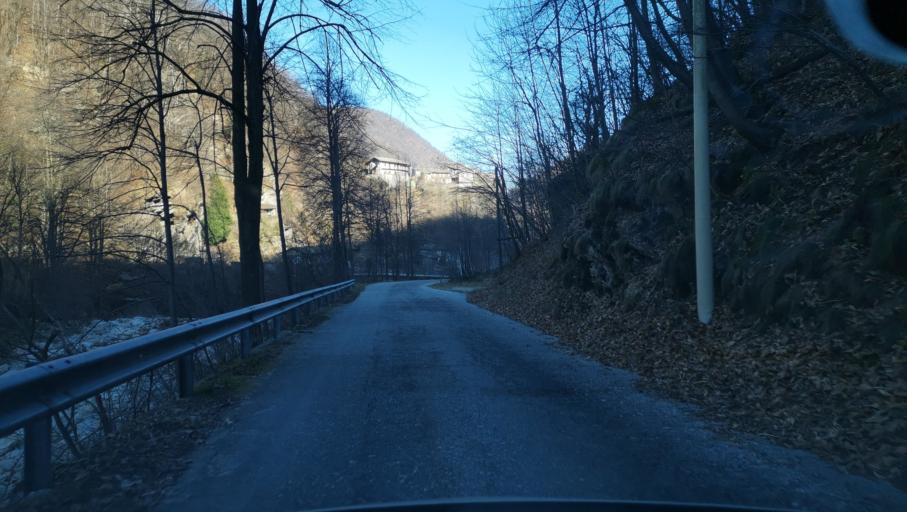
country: IT
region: Piedmont
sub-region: Provincia di Torino
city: Rora
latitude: 44.7837
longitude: 7.2091
